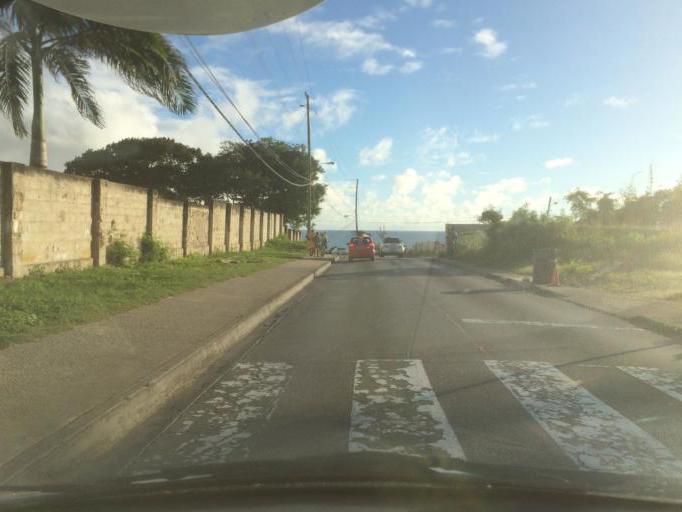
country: BB
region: Christ Church
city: Oistins
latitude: 13.0666
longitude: -59.5420
